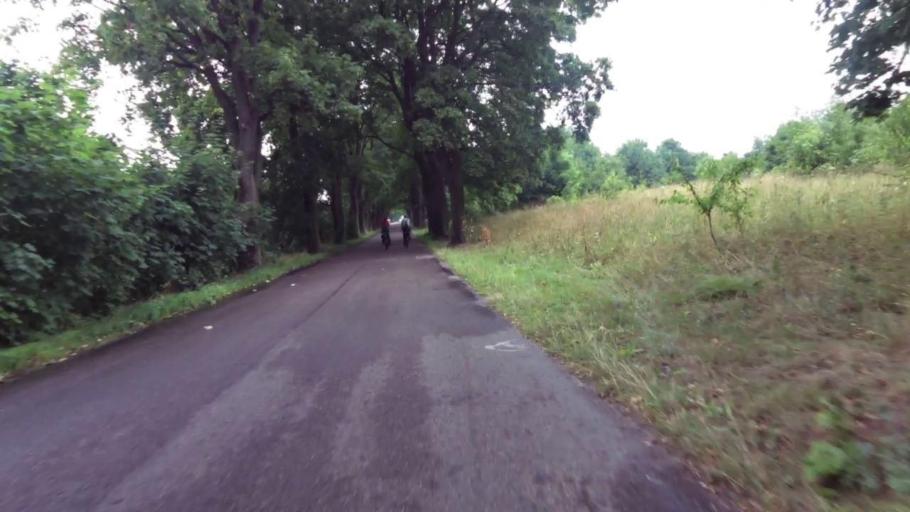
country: PL
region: West Pomeranian Voivodeship
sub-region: Powiat szczecinecki
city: Lubowo
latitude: 53.5876
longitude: 16.3805
